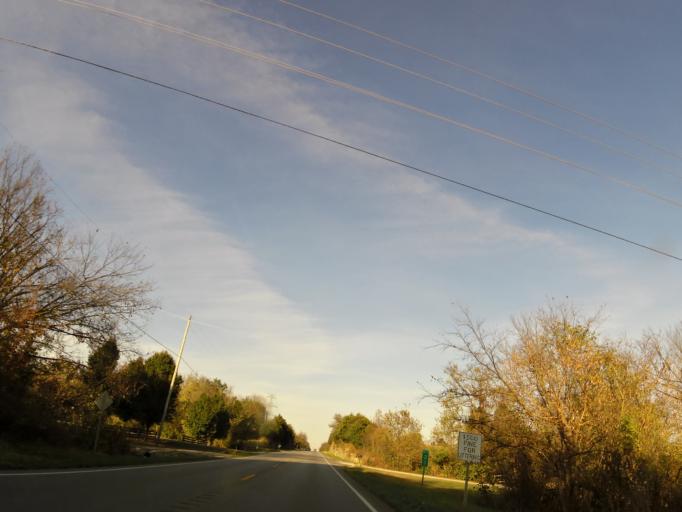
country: US
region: Kentucky
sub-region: Garrard County
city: Lancaster
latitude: 37.5719
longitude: -84.6152
